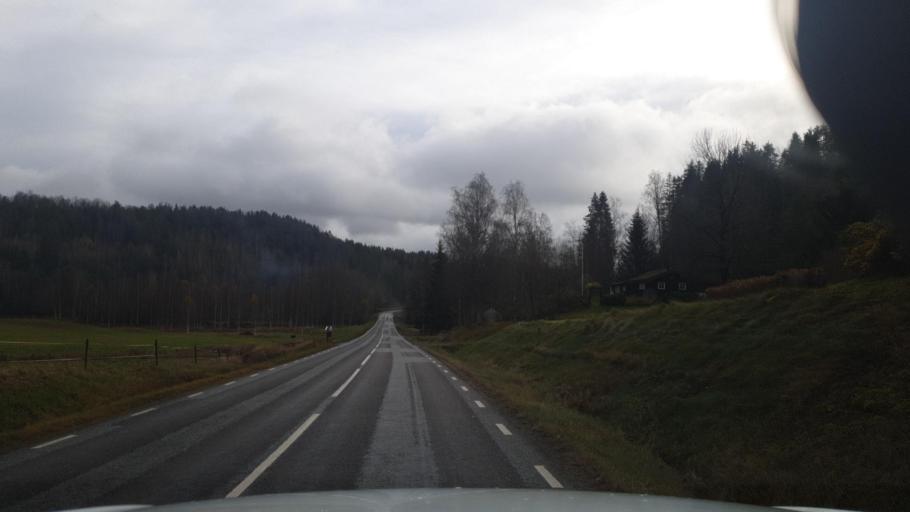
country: NO
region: Ostfold
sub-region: Romskog
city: Romskog
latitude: 59.6997
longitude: 12.0805
